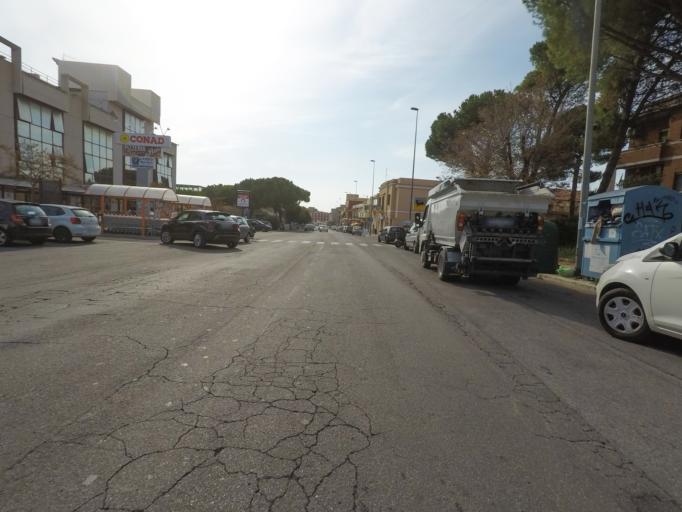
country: IT
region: Latium
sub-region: Citta metropolitana di Roma Capitale
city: Civitavecchia
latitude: 42.0981
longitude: 11.7979
